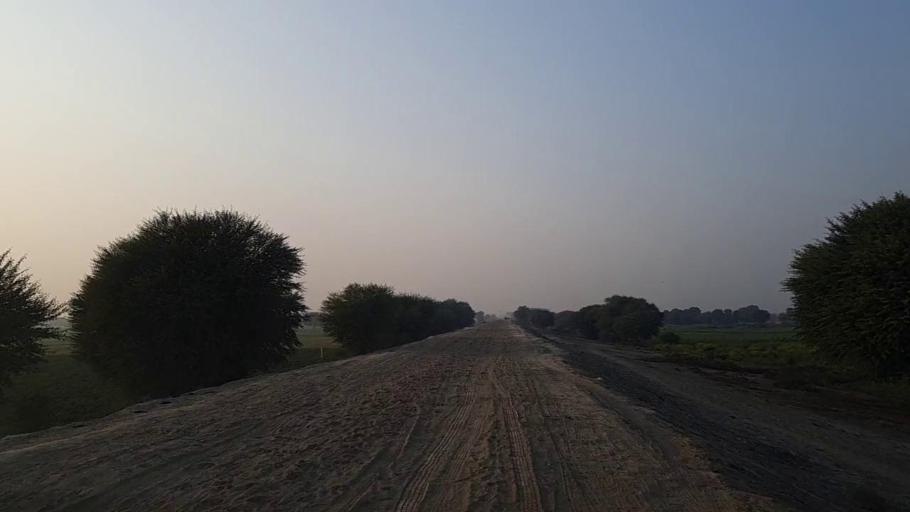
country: PK
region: Sindh
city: Sann
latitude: 26.1700
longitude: 68.1064
